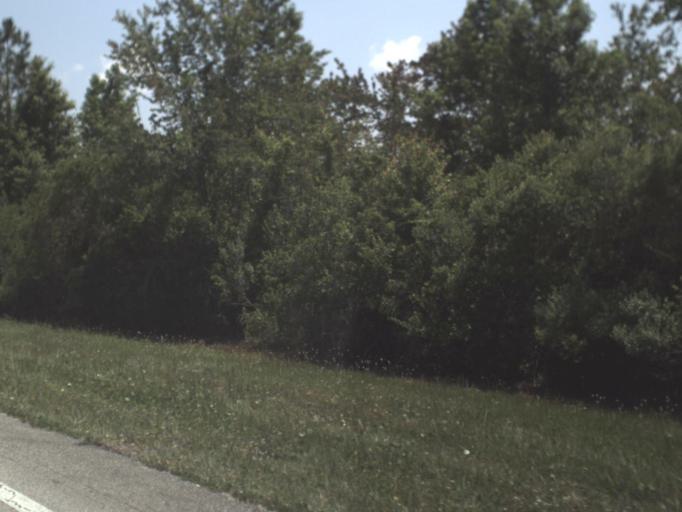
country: US
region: Florida
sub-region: Duval County
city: Baldwin
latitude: 30.2159
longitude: -82.0091
